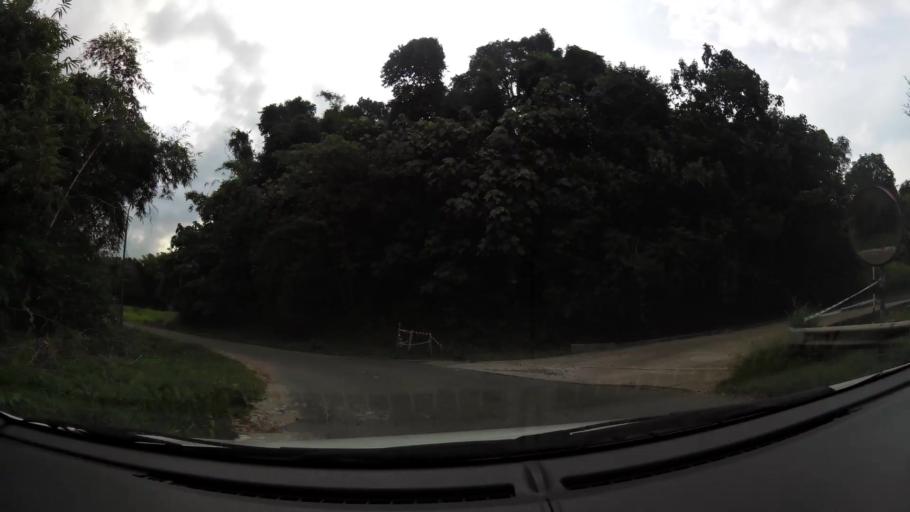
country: BN
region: Brunei and Muara
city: Bandar Seri Begawan
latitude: 4.9540
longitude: 114.9746
